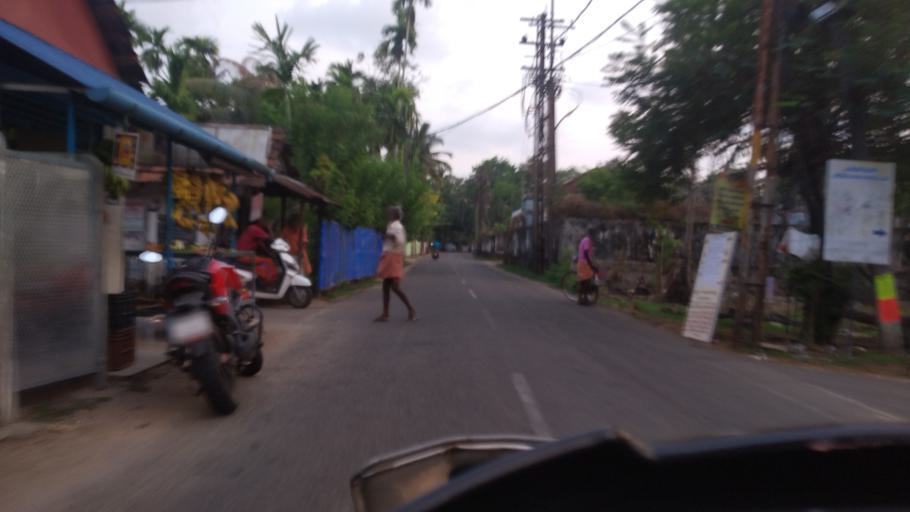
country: IN
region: Kerala
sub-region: Thrissur District
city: Kodungallur
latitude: 10.1716
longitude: 76.1985
